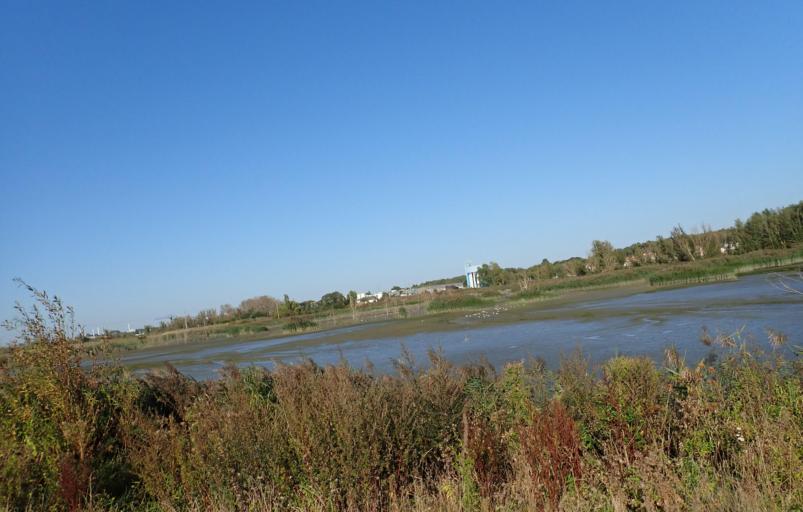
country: BE
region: Flanders
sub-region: Provincie Antwerpen
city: Hemiksem
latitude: 51.1406
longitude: 4.3217
